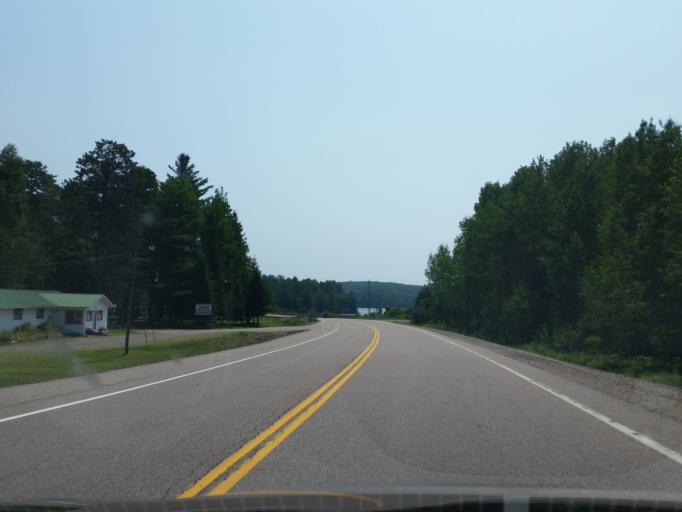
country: CA
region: Ontario
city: Deep River
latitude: 46.1701
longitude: -77.8203
